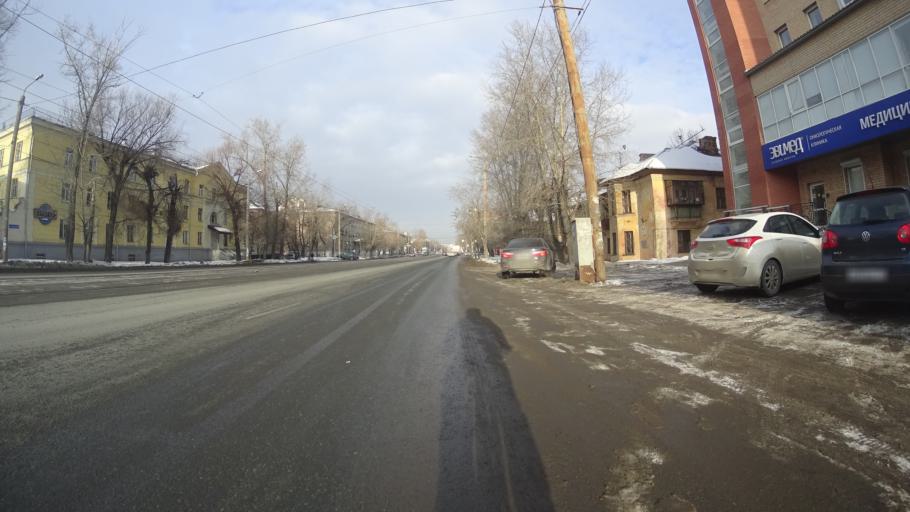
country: RU
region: Chelyabinsk
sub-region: Gorod Chelyabinsk
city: Chelyabinsk
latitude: 55.1412
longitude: 61.3819
